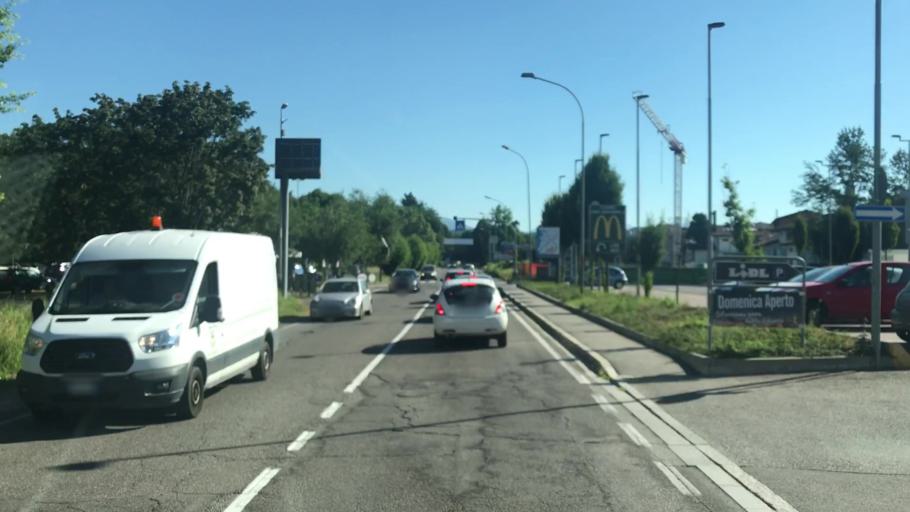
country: IT
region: Lombardy
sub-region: Provincia di Como
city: Montesolaro
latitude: 45.7381
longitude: 9.1164
